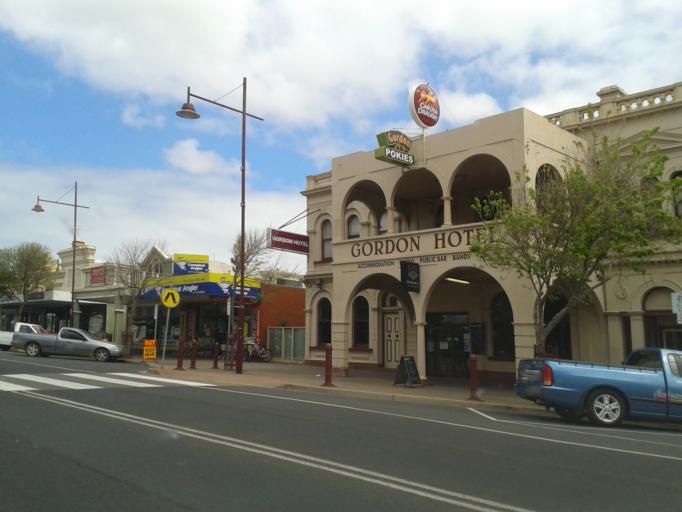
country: AU
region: Victoria
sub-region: Glenelg
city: Portland
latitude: -38.3496
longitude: 141.6063
